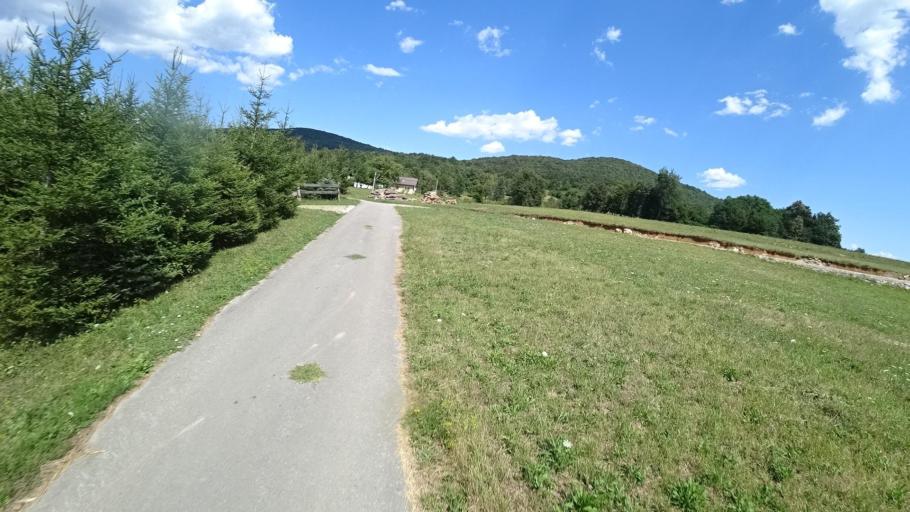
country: HR
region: Karlovacka
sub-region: Grad Ogulin
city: Ogulin
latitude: 45.2815
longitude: 15.1797
